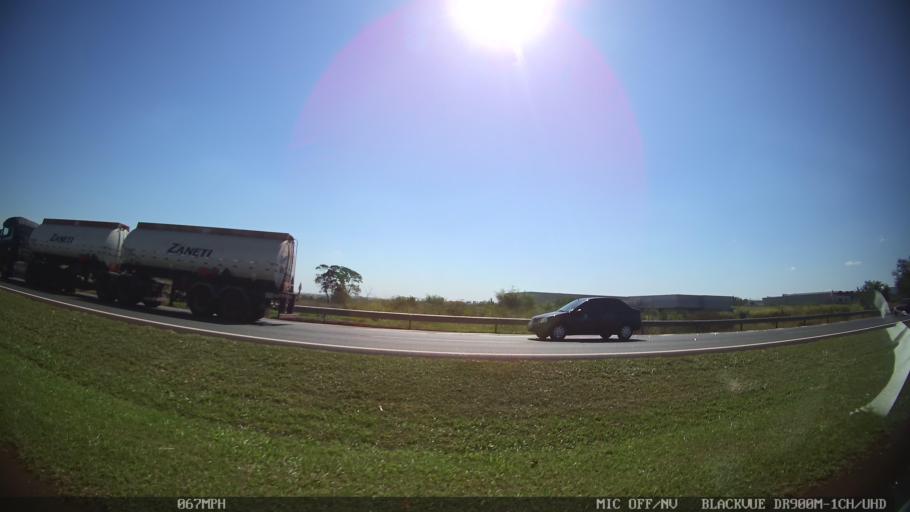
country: BR
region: Sao Paulo
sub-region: Ribeirao Preto
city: Ribeirao Preto
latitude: -21.1035
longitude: -47.8043
